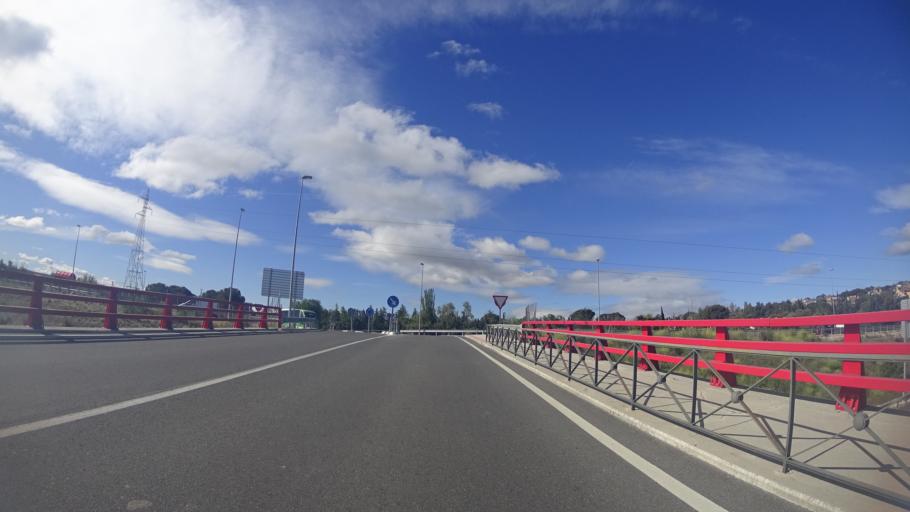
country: ES
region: Madrid
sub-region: Provincia de Madrid
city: Villanueva del Pardillo
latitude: 40.4851
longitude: -3.9402
